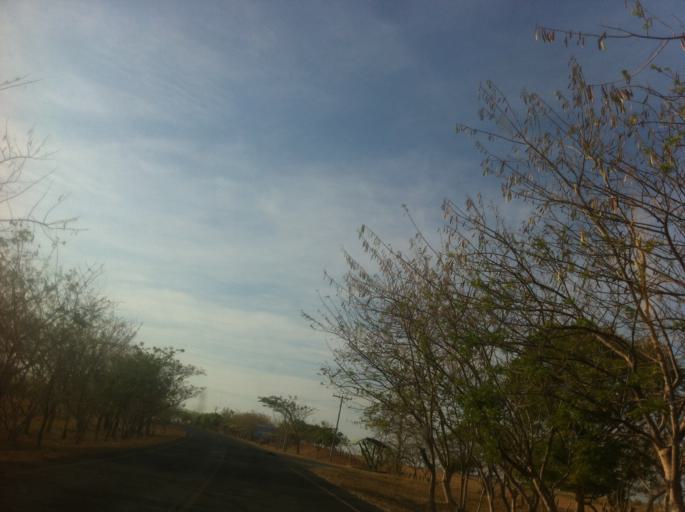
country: NI
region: Rivas
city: San Jorge
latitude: 11.3114
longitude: -85.7013
